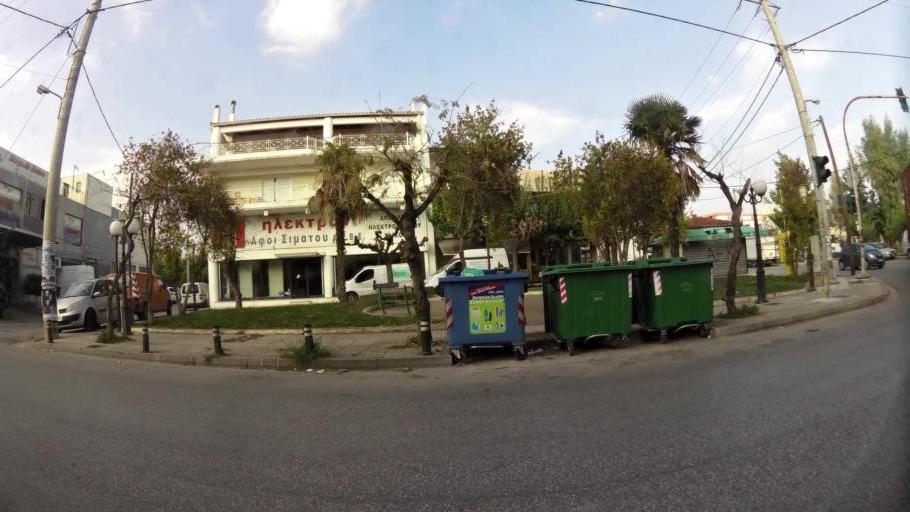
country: GR
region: Attica
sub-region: Nomarchia Anatolikis Attikis
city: Acharnes
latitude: 38.0892
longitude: 23.7430
